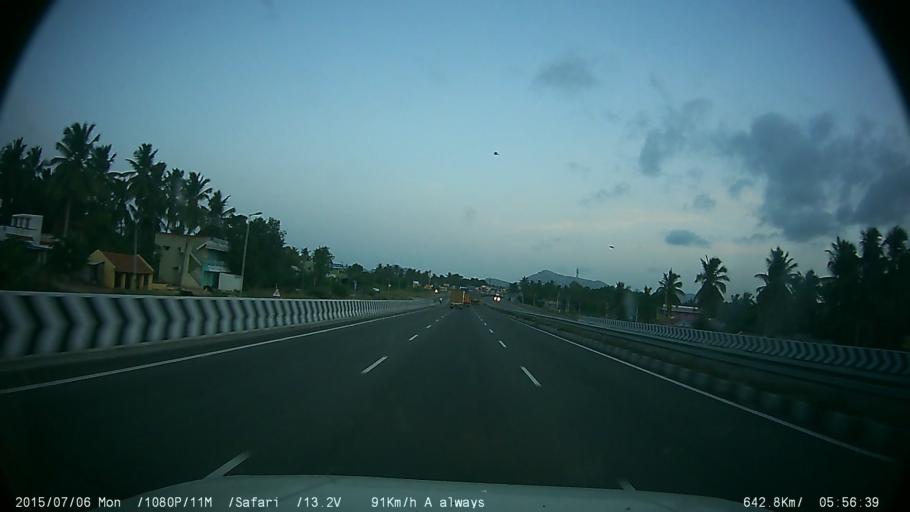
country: IN
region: Tamil Nadu
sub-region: Krishnagiri
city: Krishnagiri
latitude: 12.5760
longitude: 78.1671
